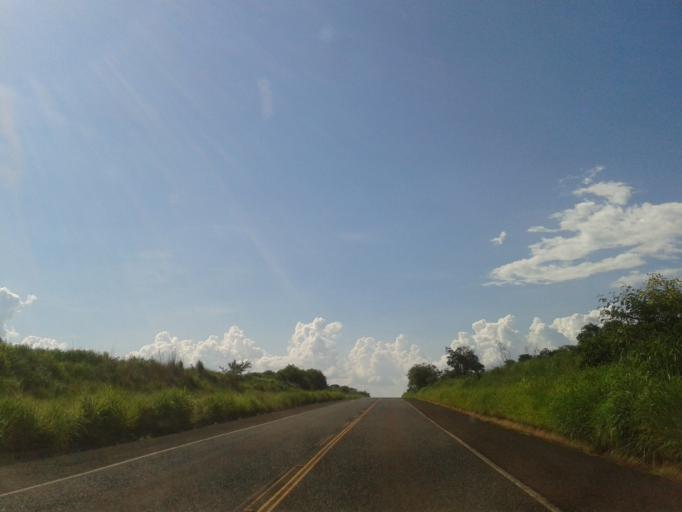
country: BR
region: Minas Gerais
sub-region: Santa Vitoria
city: Santa Vitoria
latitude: -19.0507
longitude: -50.4002
